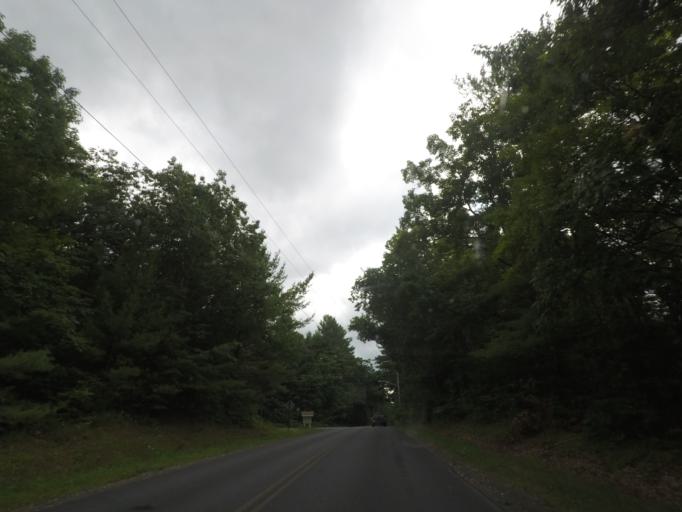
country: US
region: New York
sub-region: Saratoga County
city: Stillwater
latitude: 42.8672
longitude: -73.5555
